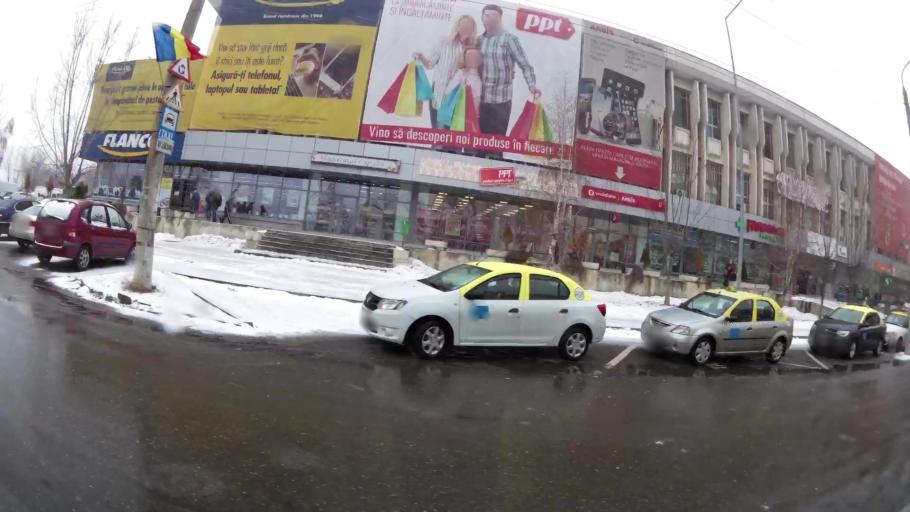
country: RO
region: Dambovita
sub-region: Municipiul Targoviste
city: Targoviste
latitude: 44.9195
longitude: 25.4522
